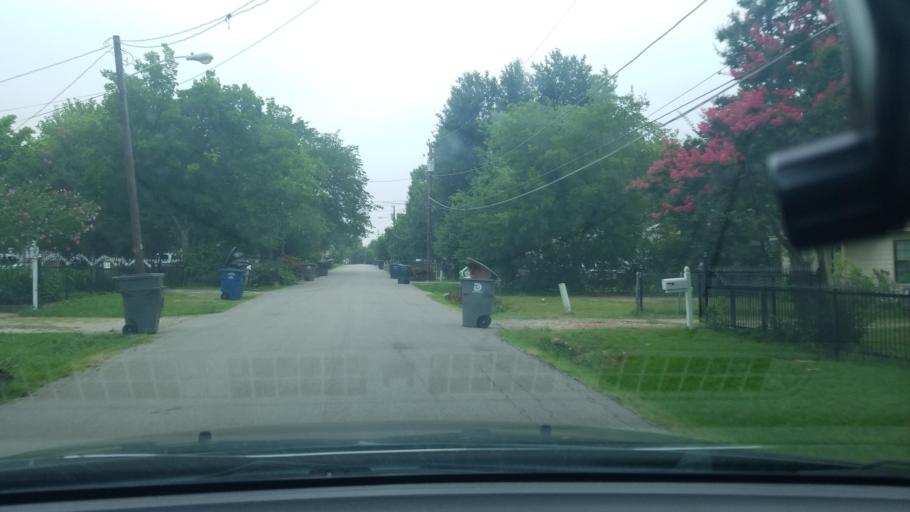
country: US
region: Texas
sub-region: Dallas County
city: Balch Springs
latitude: 32.7610
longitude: -96.6766
